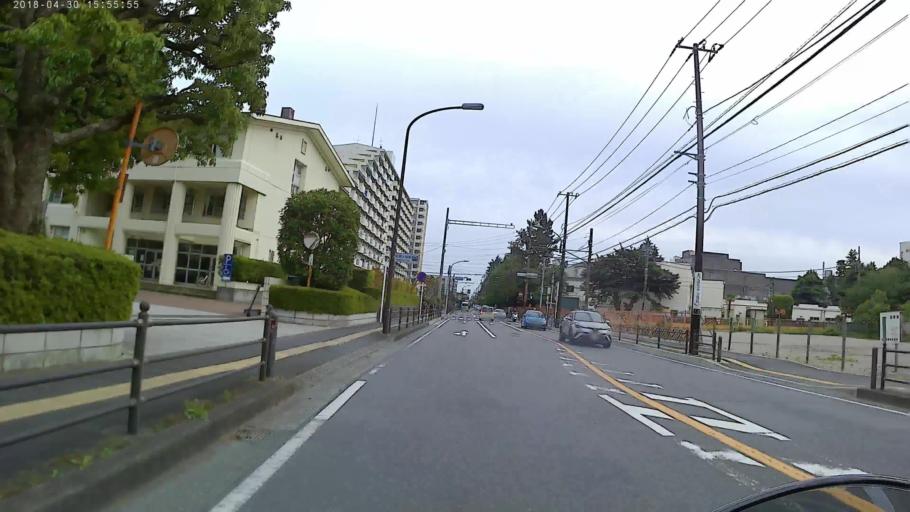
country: JP
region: Tokyo
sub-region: Machida-shi
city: Machida
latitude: 35.5361
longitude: 139.4302
